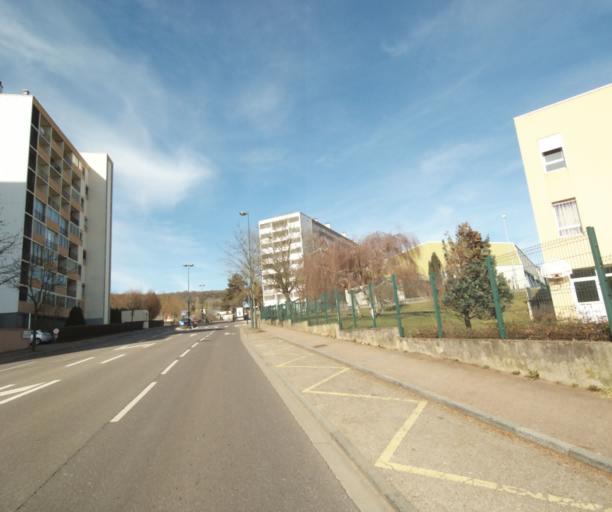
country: FR
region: Lorraine
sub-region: Departement de Meurthe-et-Moselle
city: Laxou
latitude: 48.6779
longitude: 6.1453
